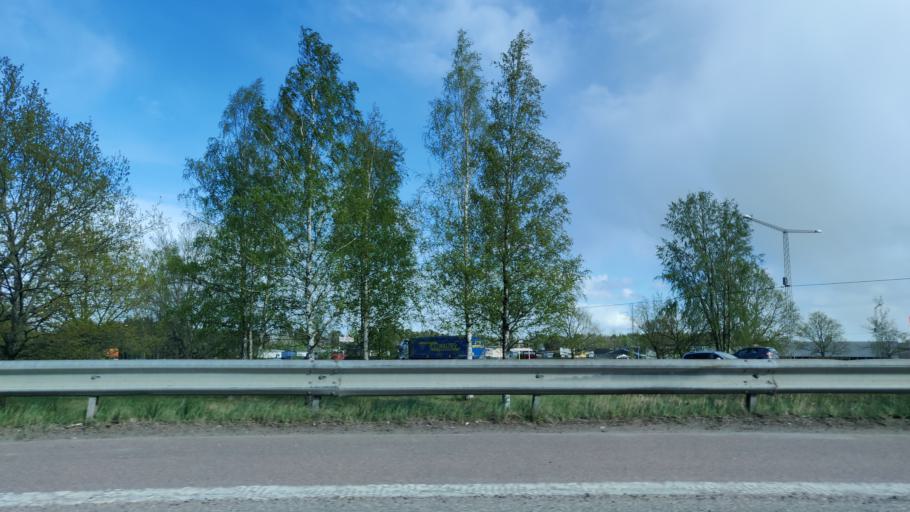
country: SE
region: Vaermland
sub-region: Karlstads Kommun
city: Karlstad
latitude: 59.3795
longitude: 13.4433
